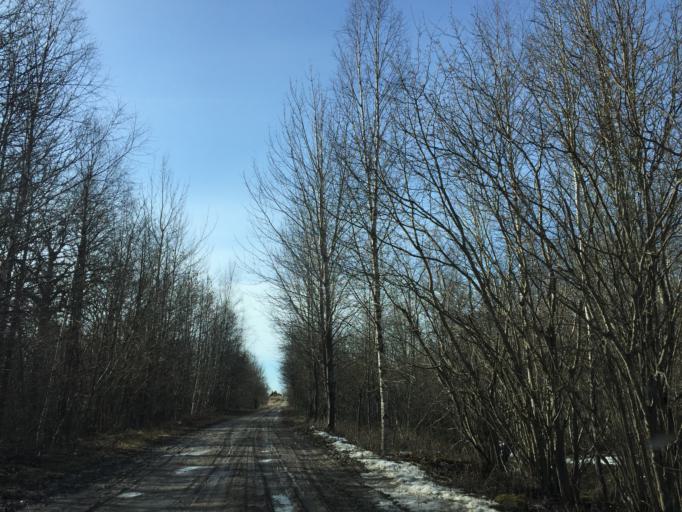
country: EE
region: Laeaene
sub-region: Haapsalu linn
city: Haapsalu
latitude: 58.6557
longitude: 23.5148
